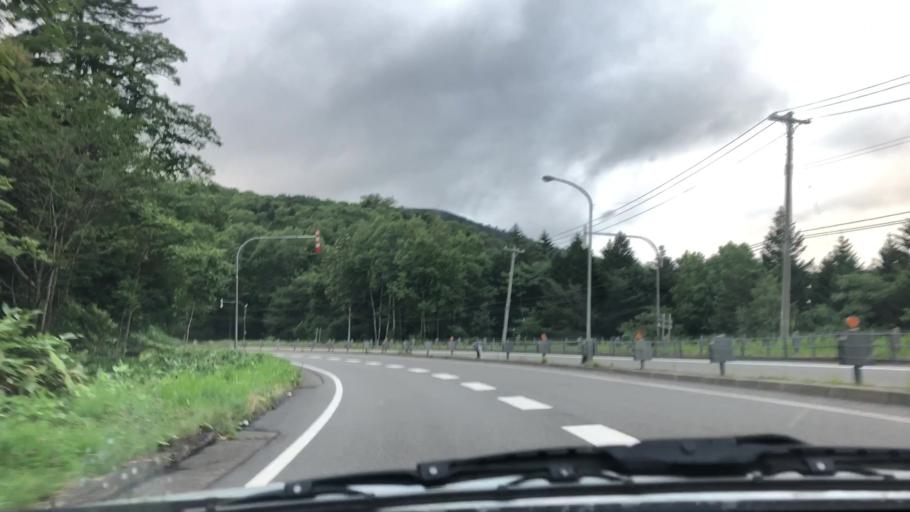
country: JP
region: Hokkaido
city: Shimo-furano
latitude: 42.9119
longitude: 142.3656
